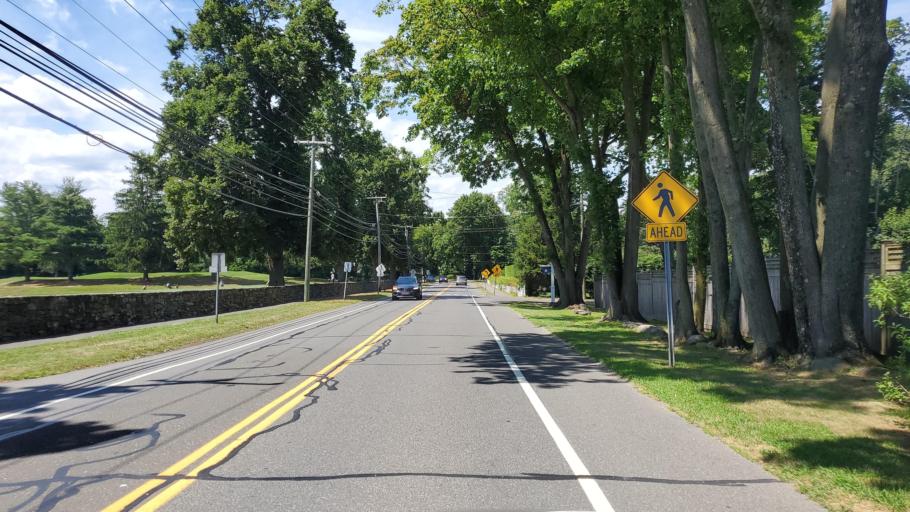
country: US
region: Connecticut
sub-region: Fairfield County
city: Westport
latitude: 41.1142
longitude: -73.3582
